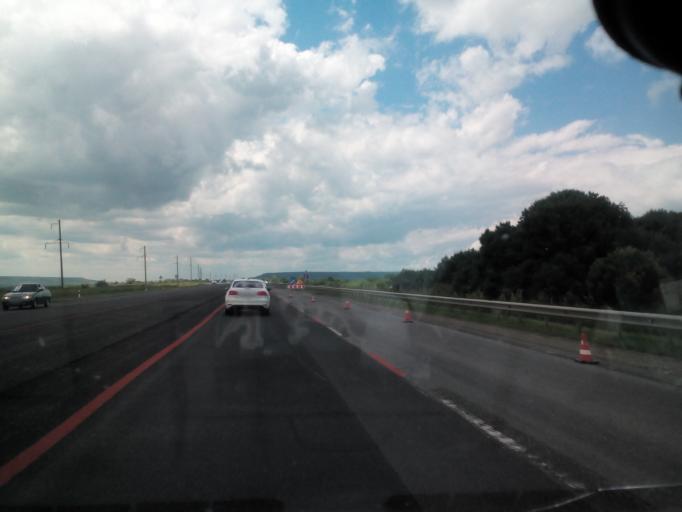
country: RU
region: Stavropol'skiy
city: Tatarka
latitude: 44.9530
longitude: 41.9684
